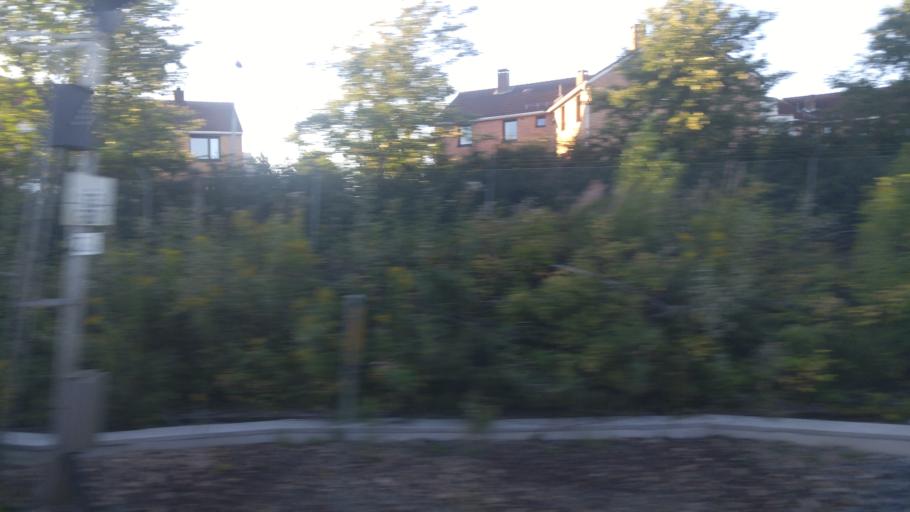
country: NO
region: Akershus
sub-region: Lorenskog
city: Kjenn
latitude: 59.9524
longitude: 10.8906
